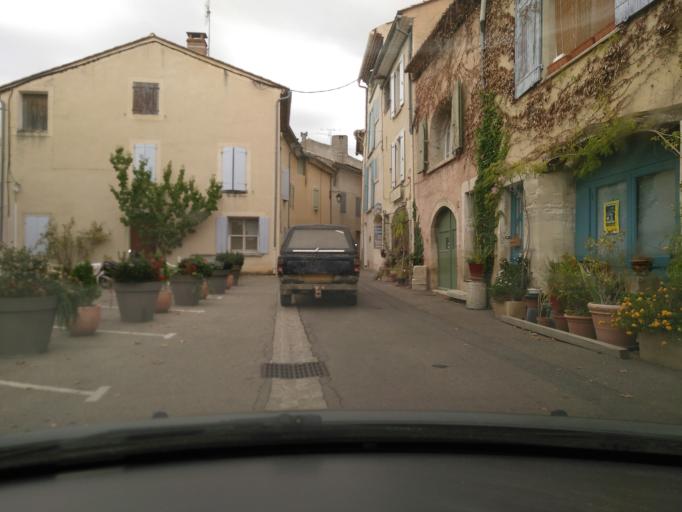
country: FR
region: Rhone-Alpes
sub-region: Departement de la Drome
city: Vinsobres
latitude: 44.3333
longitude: 5.0612
